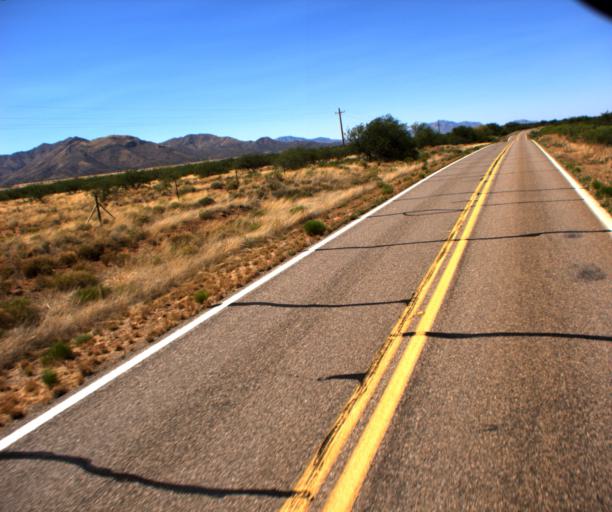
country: US
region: Arizona
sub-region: Pima County
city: Three Points
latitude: 31.7262
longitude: -111.4879
